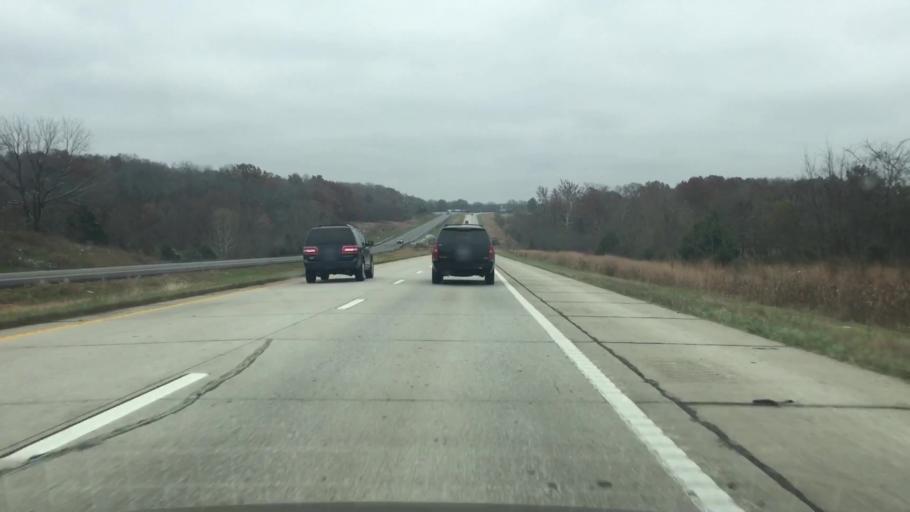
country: US
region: Missouri
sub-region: Saint Clair County
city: Osceola
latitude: 38.0199
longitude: -93.6677
